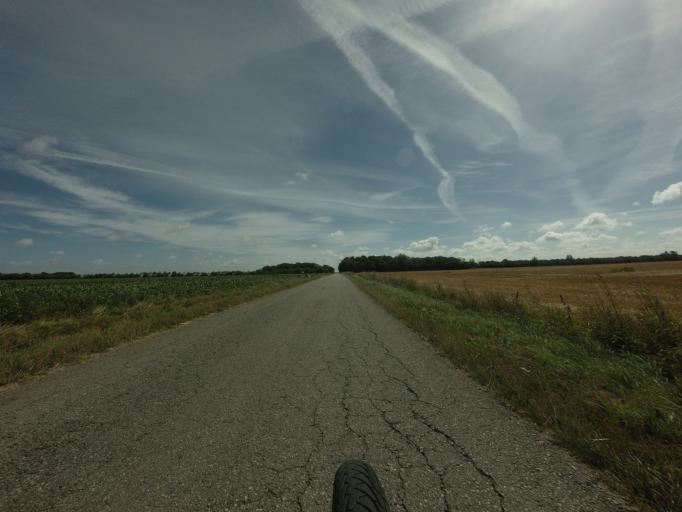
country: DK
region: North Denmark
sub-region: Jammerbugt Kommune
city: Pandrup
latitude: 57.3429
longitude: 9.7799
